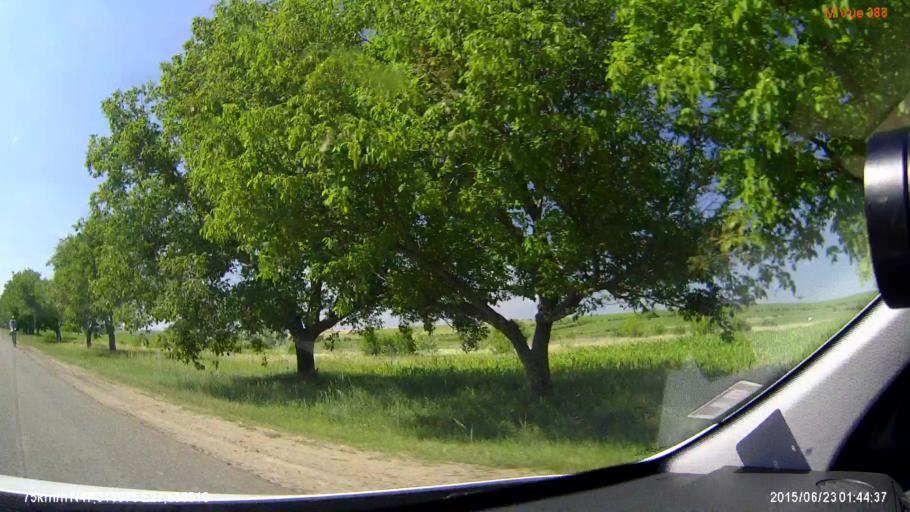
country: RO
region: Iasi
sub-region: Comuna Victoria
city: Victoria
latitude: 47.3169
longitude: 27.6588
